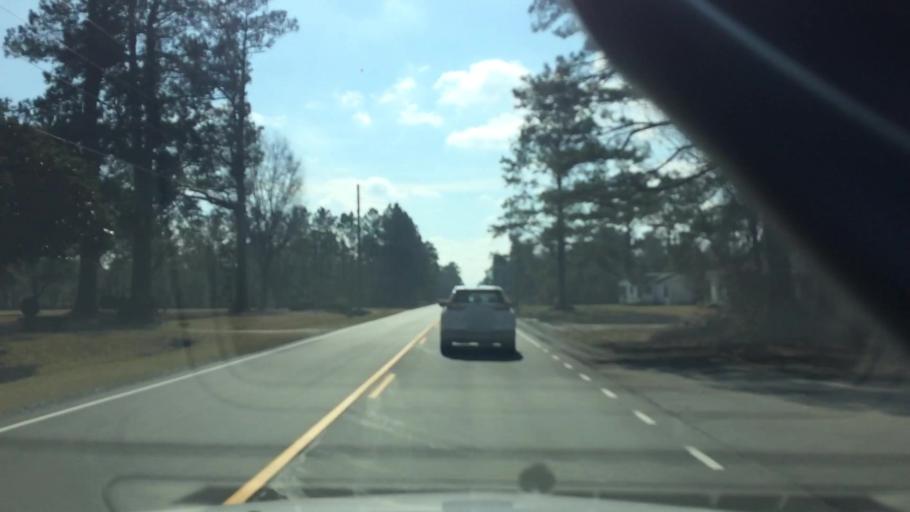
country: US
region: North Carolina
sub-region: Duplin County
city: Beulaville
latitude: 34.9796
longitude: -77.7601
